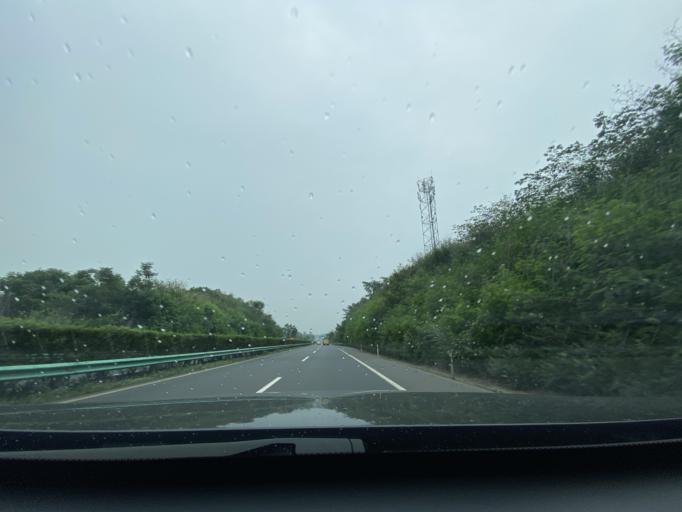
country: CN
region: Sichuan
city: Longquan
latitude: 30.3241
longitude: 104.1209
